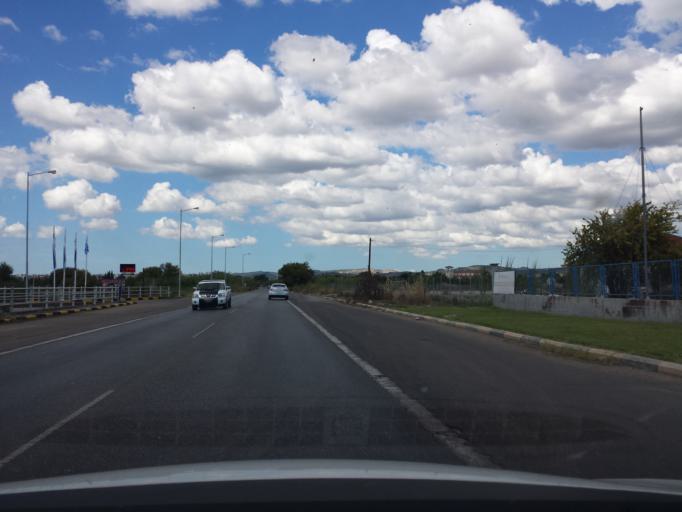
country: GR
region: West Greece
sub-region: Nomos Ileias
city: Pyrgos
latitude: 37.6589
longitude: 21.4636
